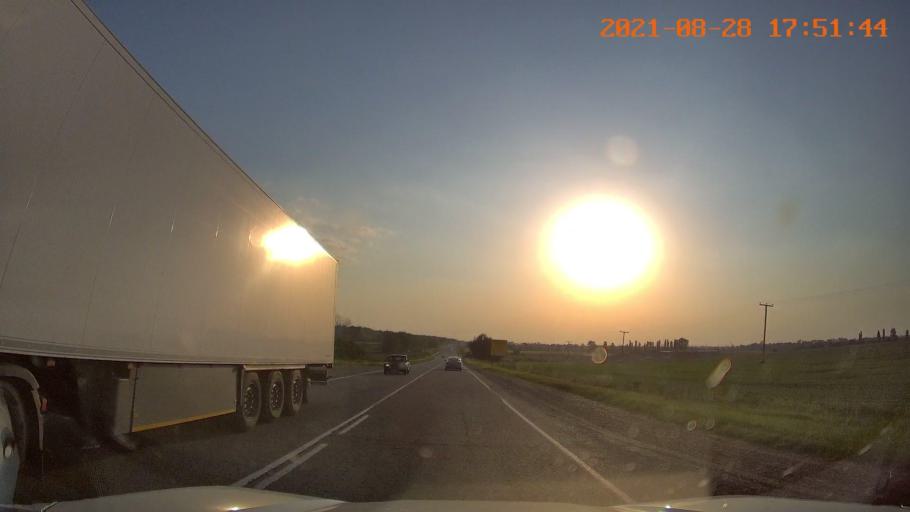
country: RU
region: Krasnodarskiy
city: Konstantinovskaya
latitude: 44.9426
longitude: 40.7865
